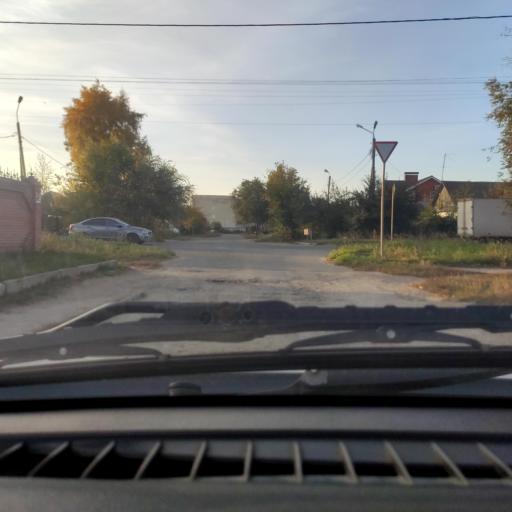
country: RU
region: Samara
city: Tol'yatti
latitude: 53.5372
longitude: 49.4036
